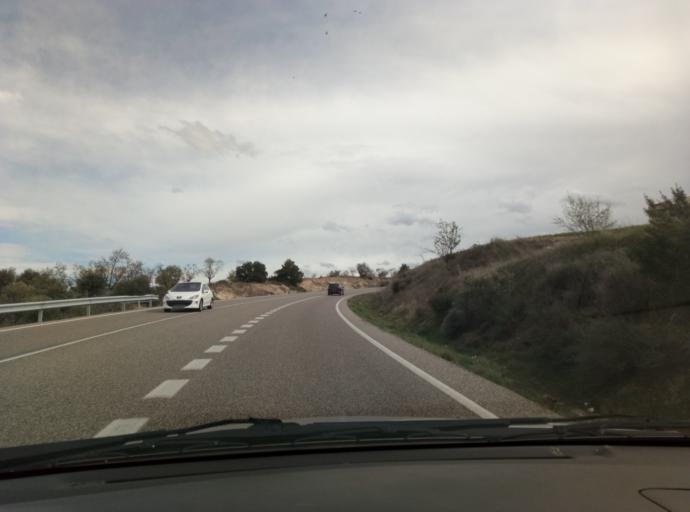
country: ES
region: Catalonia
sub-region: Provincia de Lleida
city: Ciutadilla
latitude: 41.5560
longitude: 1.1369
